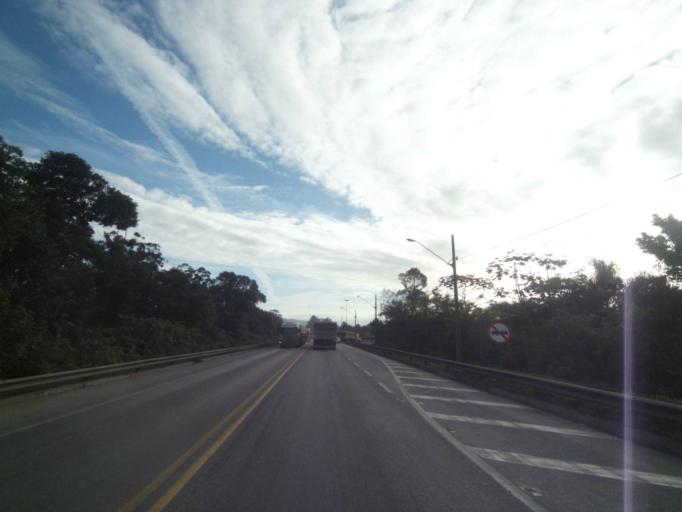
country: BR
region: Parana
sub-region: Paranagua
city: Paranagua
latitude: -25.5476
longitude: -48.5605
